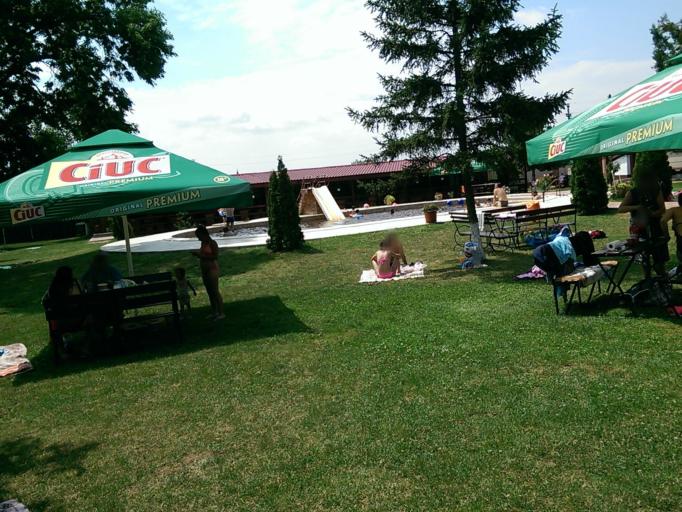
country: RO
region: Bihor
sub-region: Comuna Madaras
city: Madaras
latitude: 46.8353
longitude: 21.6762
